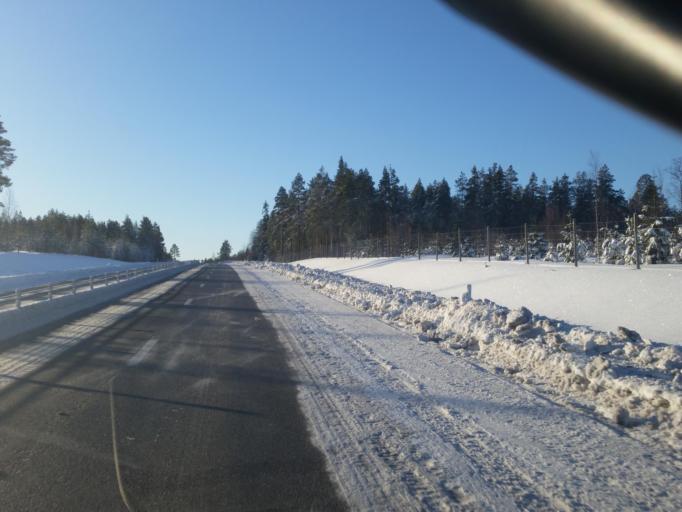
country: SE
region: Norrbotten
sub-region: Pitea Kommun
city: Pitea
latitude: 65.1974
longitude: 21.5118
